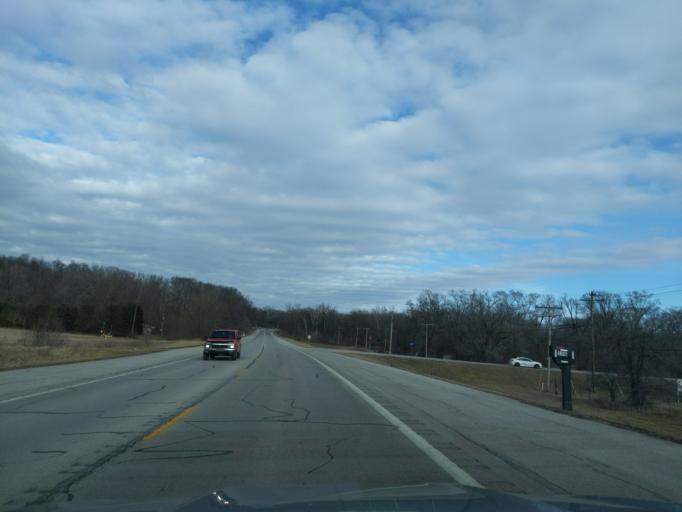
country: US
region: Indiana
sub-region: Tippecanoe County
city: Shadeland
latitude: 40.3783
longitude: -86.9391
